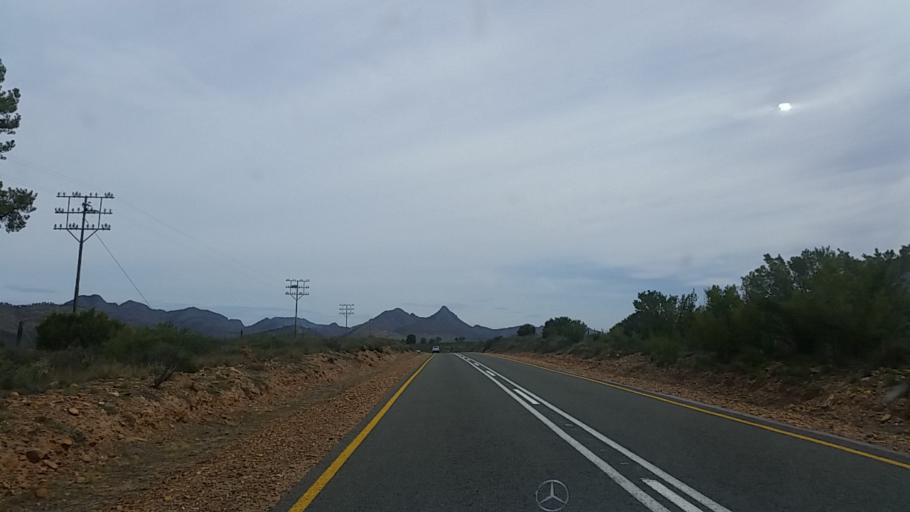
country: ZA
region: Western Cape
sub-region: Eden District Municipality
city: George
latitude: -33.8198
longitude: 22.4969
